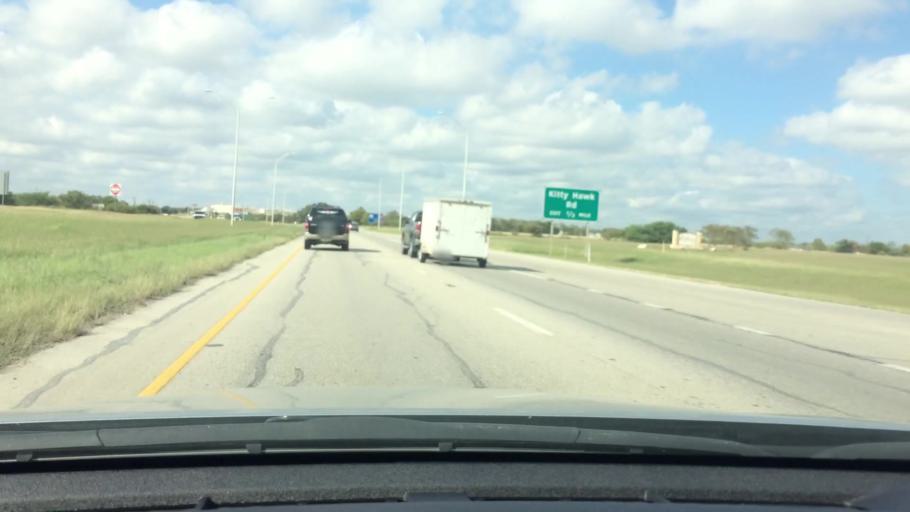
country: US
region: Texas
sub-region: Bexar County
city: Universal City
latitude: 29.5397
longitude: -98.3060
